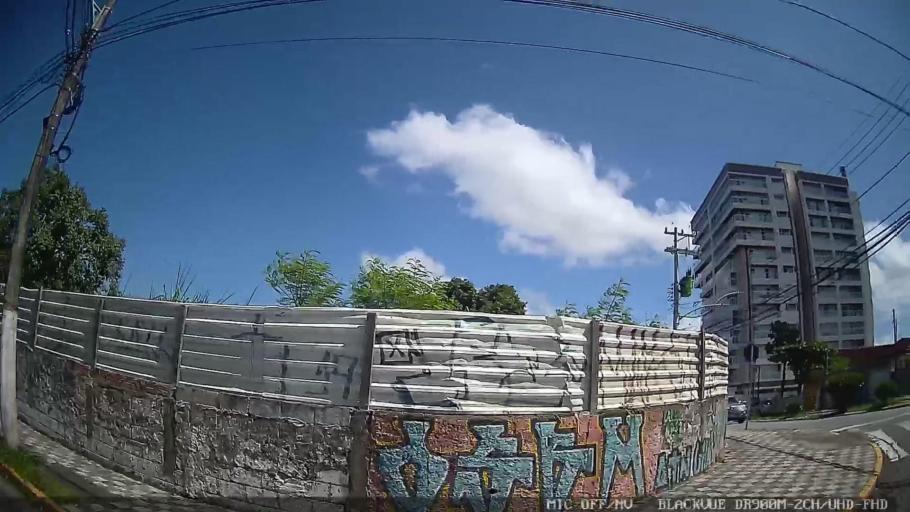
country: BR
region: Sao Paulo
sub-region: Peruibe
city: Peruibe
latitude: -24.3236
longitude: -46.9988
